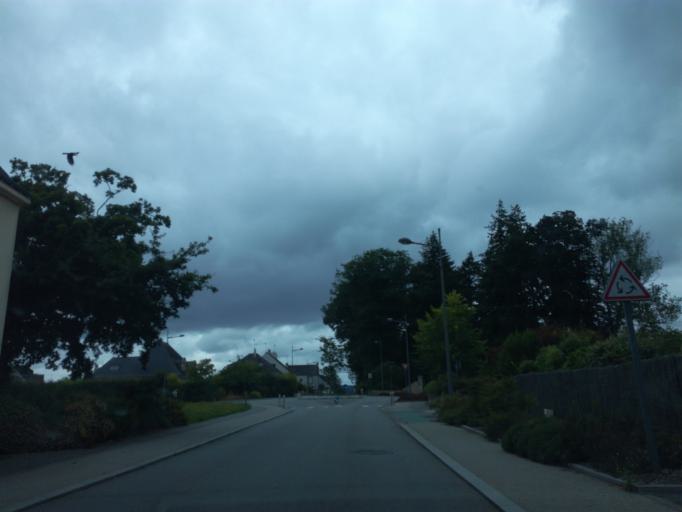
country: FR
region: Brittany
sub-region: Departement du Morbihan
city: Pontivy
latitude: 48.0678
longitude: -2.9507
